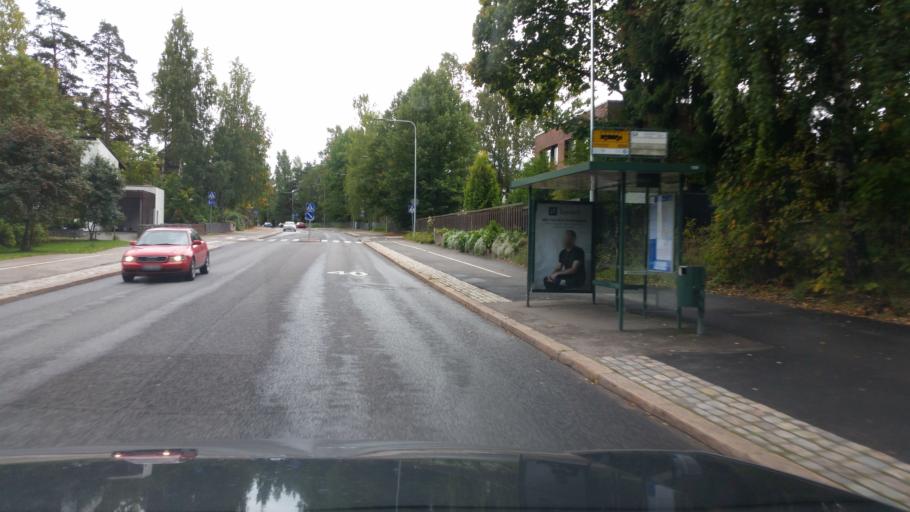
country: FI
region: Uusimaa
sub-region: Helsinki
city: Helsinki
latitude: 60.2375
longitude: 24.9636
